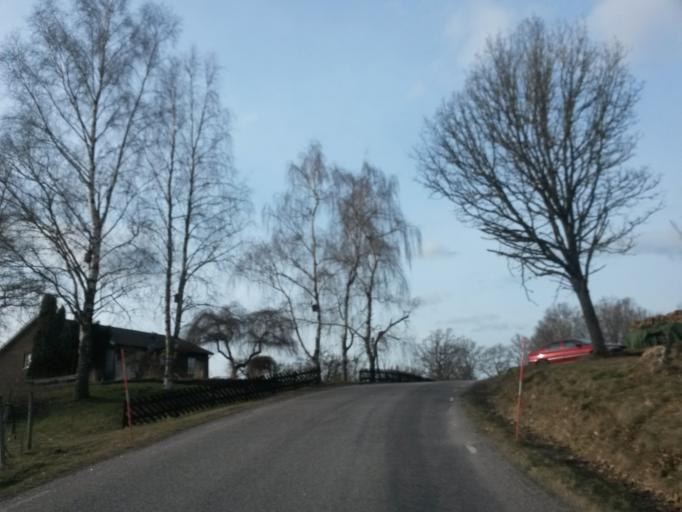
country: SE
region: Vaestra Goetaland
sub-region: Vargarda Kommun
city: Jonstorp
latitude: 57.9958
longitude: 12.7663
